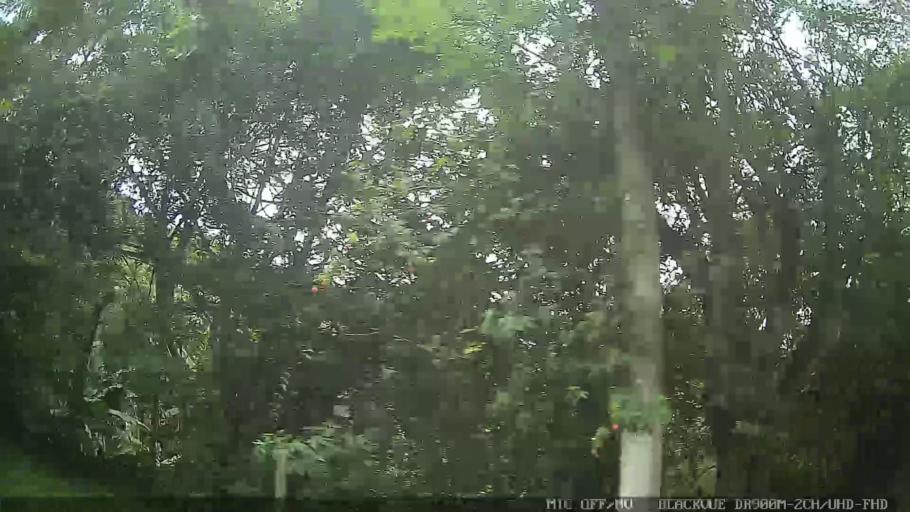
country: BR
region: Sao Paulo
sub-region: Aruja
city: Aruja
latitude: -23.4170
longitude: -46.3392
